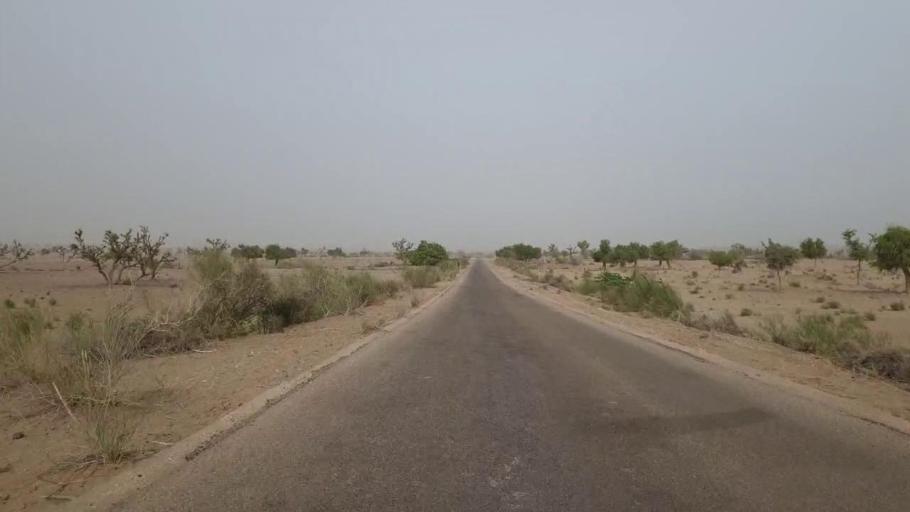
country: PK
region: Sindh
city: Islamkot
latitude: 24.5502
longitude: 70.3558
